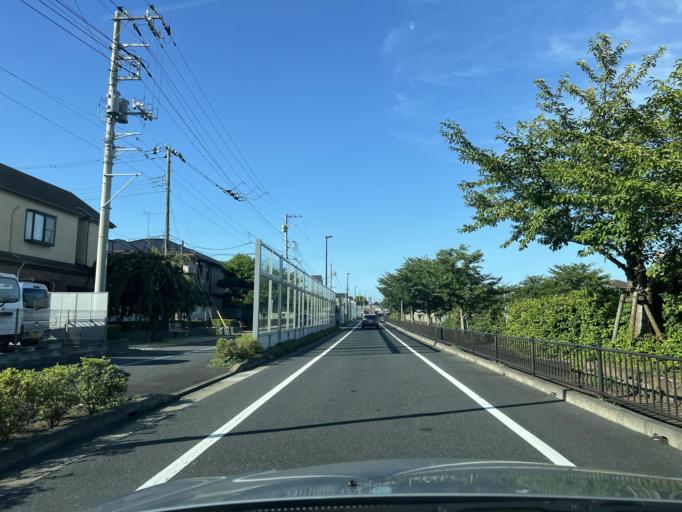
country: JP
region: Chiba
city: Funabashi
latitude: 35.7290
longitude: 139.9398
